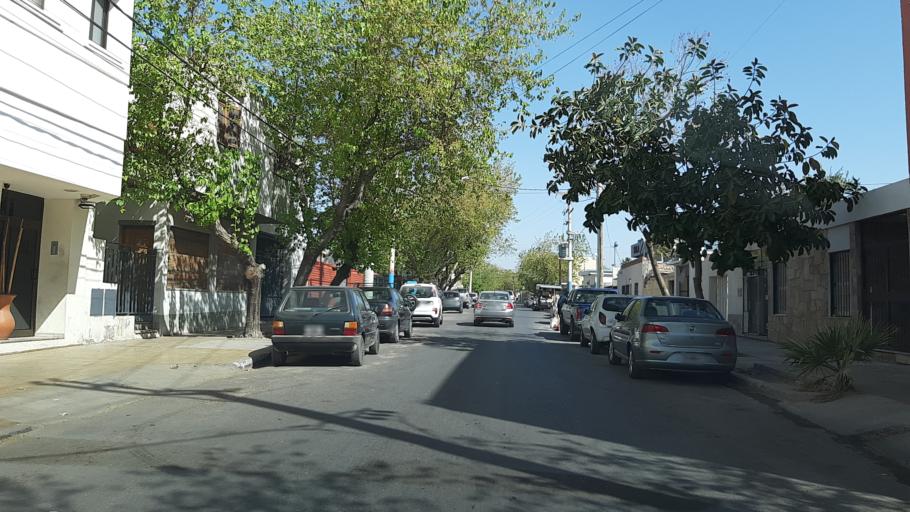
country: AR
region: San Juan
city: San Juan
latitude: -31.5311
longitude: -68.5324
